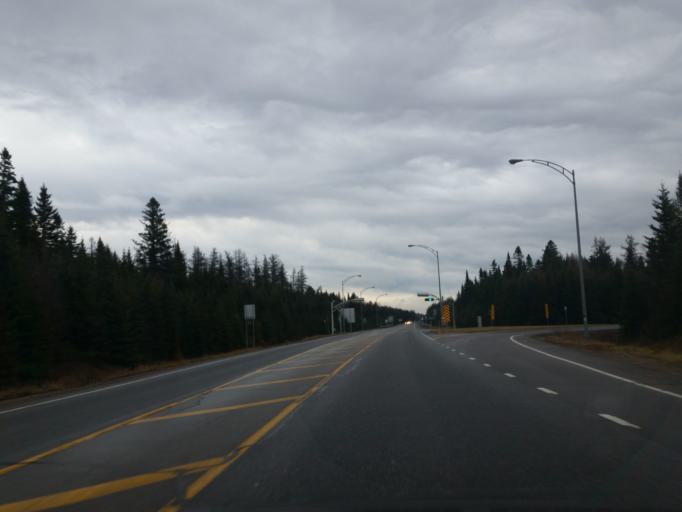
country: CA
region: Quebec
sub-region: Capitale-Nationale
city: Shannon
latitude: 46.8807
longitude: -71.4693
